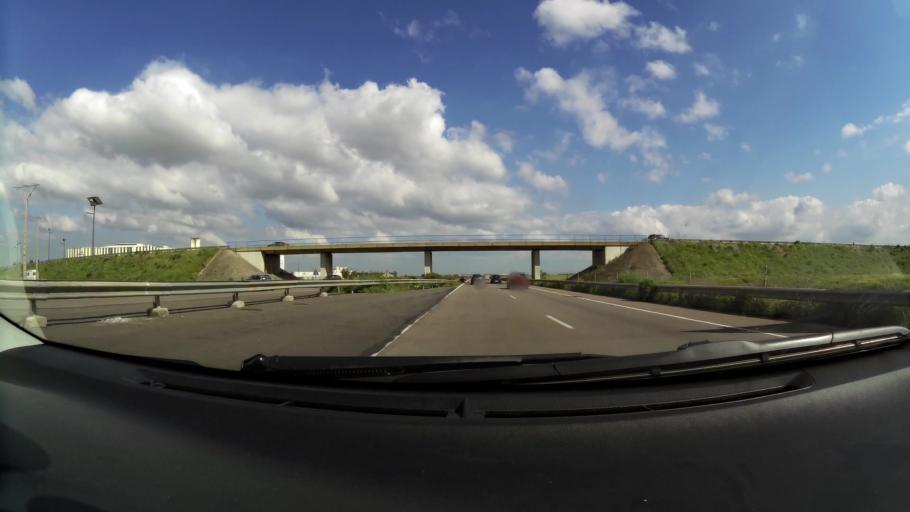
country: MA
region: Chaouia-Ouardigha
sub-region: Settat Province
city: Berrechid
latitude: 33.3125
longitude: -7.5952
